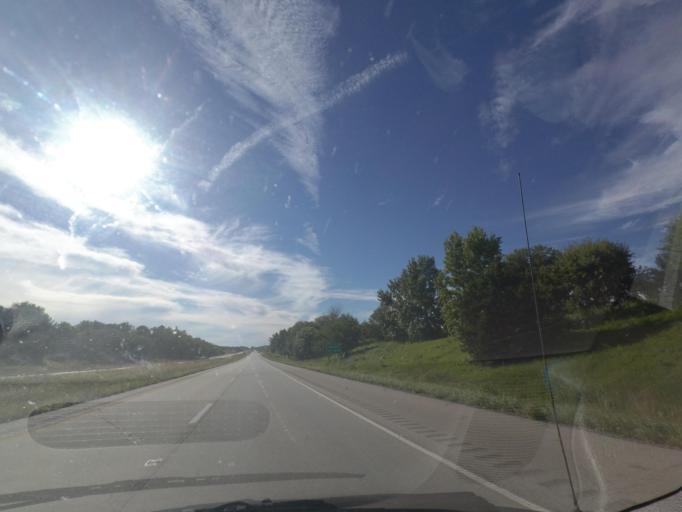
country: US
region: Illinois
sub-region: Macon County
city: Forsyth
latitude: 39.9088
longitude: -88.9449
